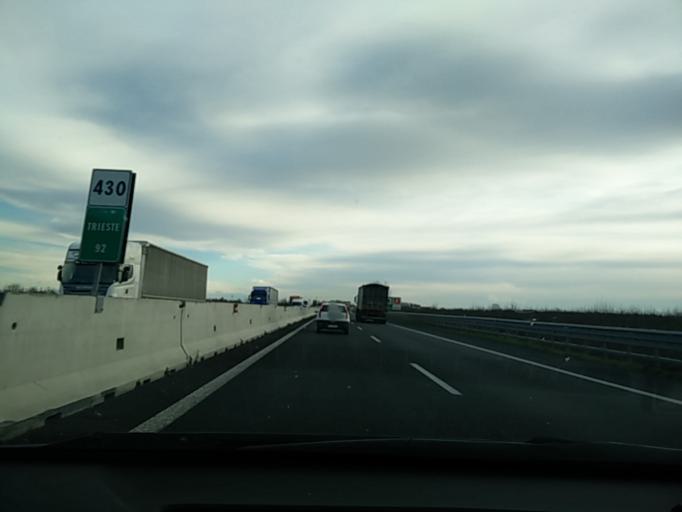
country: IT
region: Veneto
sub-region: Provincia di Treviso
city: Cessalto
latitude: 45.6972
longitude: 12.5857
